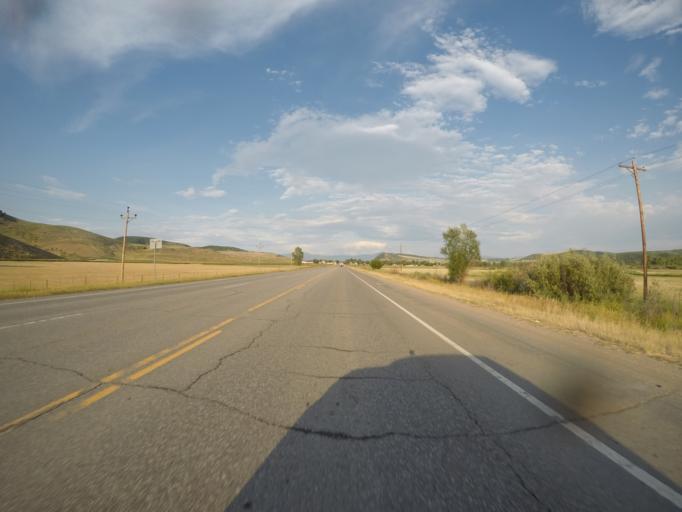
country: US
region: Colorado
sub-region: Routt County
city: Steamboat Springs
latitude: 40.4857
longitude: -107.0337
